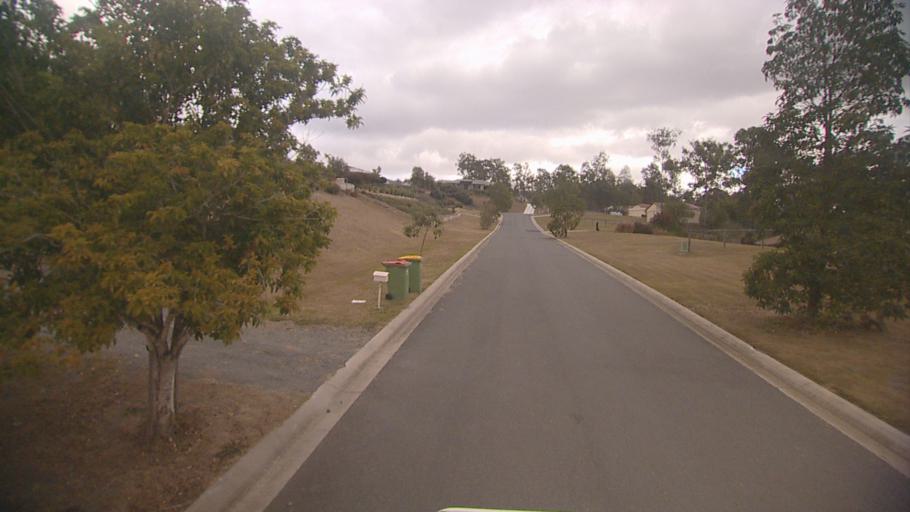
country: AU
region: Queensland
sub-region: Logan
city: Cedar Vale
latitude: -27.8656
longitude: 153.0799
